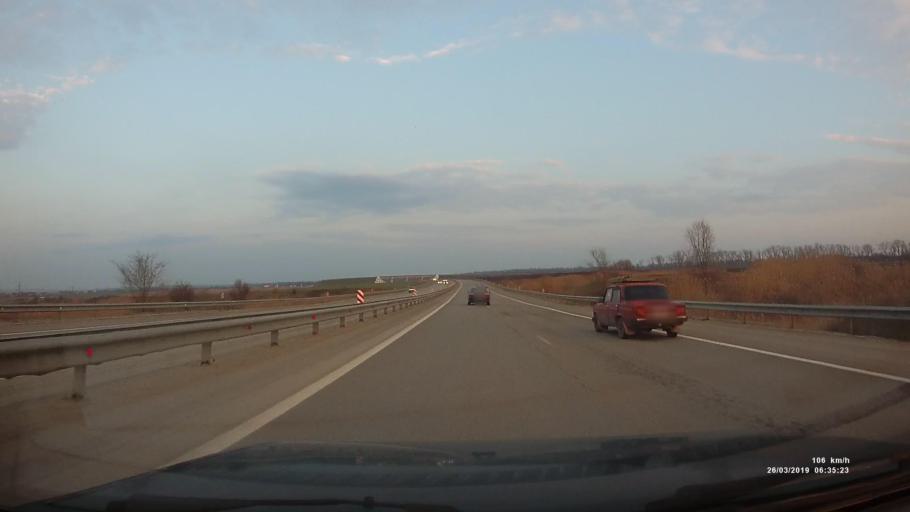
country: RU
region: Rostov
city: Chaltyr
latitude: 47.2807
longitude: 39.4457
